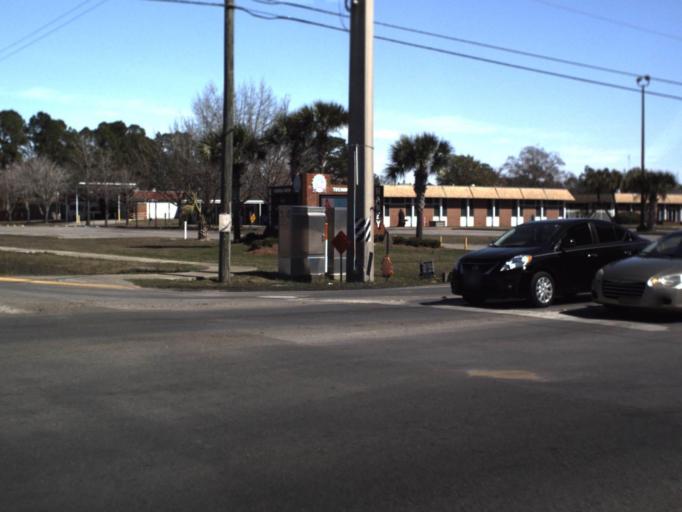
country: US
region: Florida
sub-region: Bay County
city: Hiland Park
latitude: 30.2022
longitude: -85.6496
